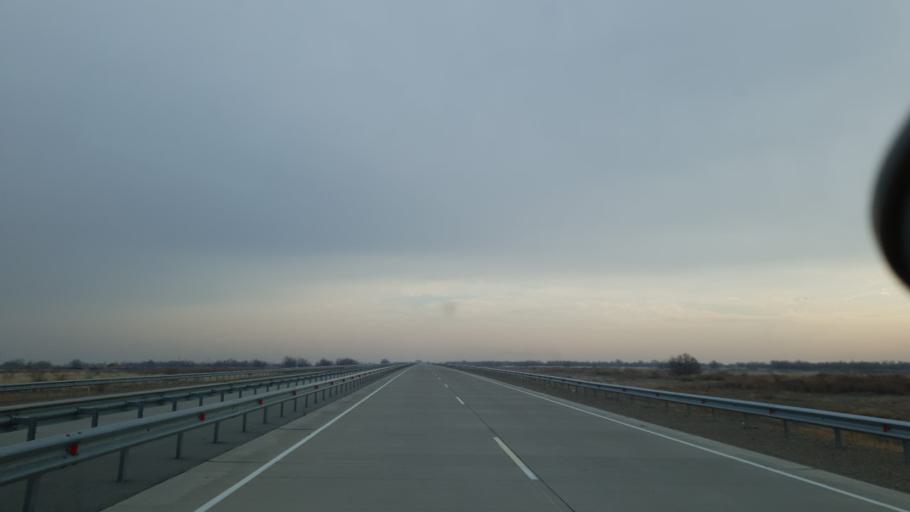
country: KZ
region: Almaty Oblysy
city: Zharkent
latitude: 44.0166
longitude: 79.7839
